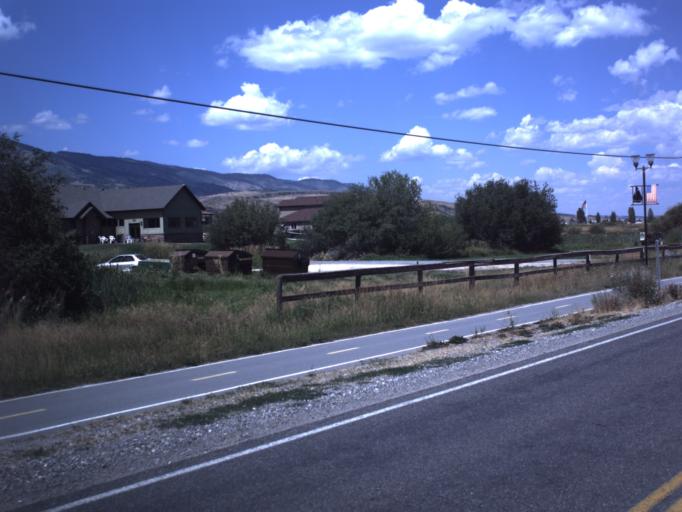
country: US
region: Idaho
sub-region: Bear Lake County
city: Paris
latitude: 41.9288
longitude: -111.3966
